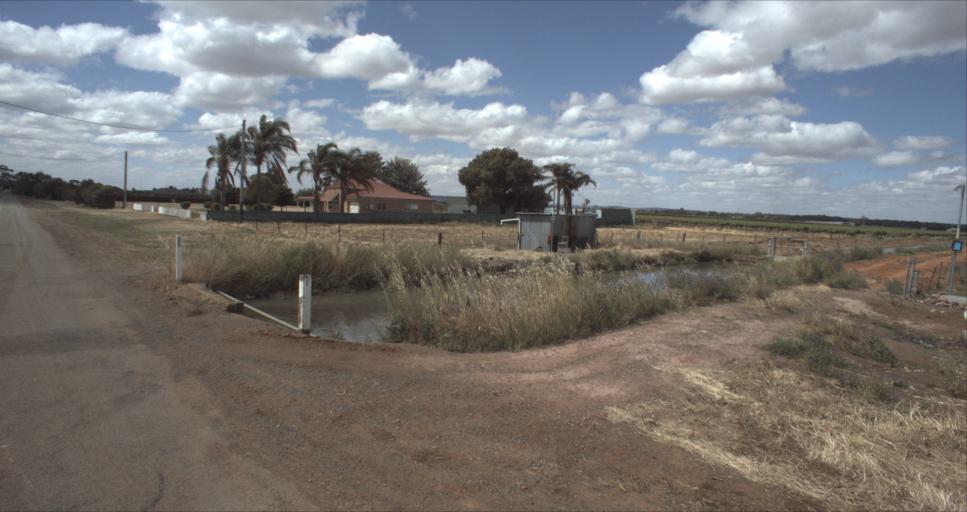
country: AU
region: New South Wales
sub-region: Leeton
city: Leeton
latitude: -34.5844
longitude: 146.3963
